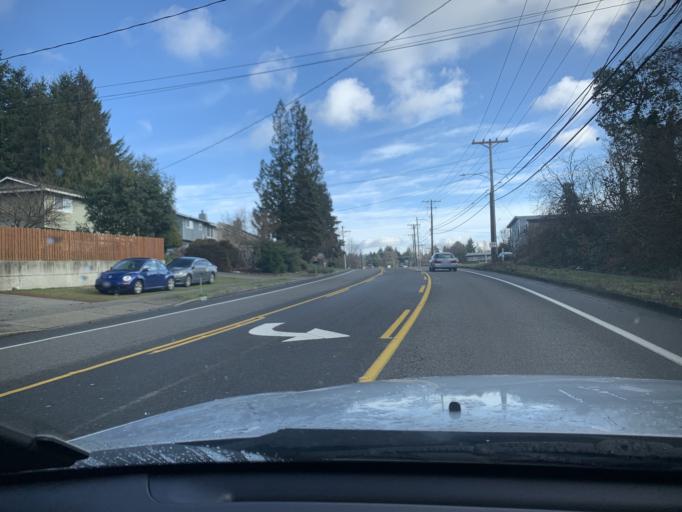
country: US
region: Washington
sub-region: Pierce County
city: Fircrest
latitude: 47.2716
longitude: -122.5274
